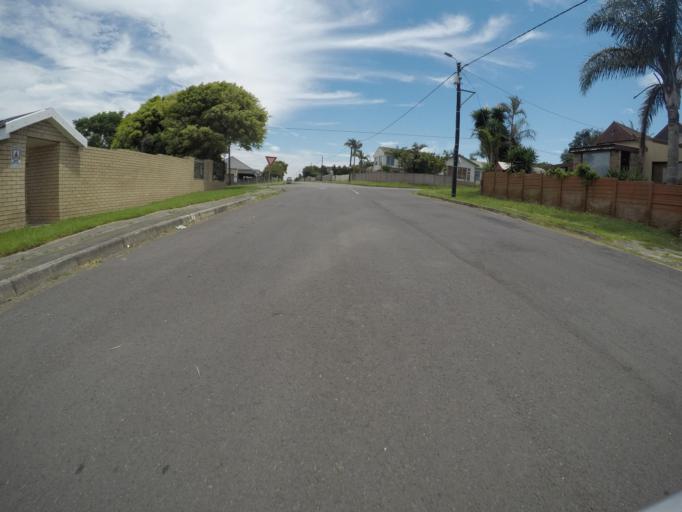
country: ZA
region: Eastern Cape
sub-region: Buffalo City Metropolitan Municipality
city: East London
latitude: -33.0384
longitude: 27.8528
